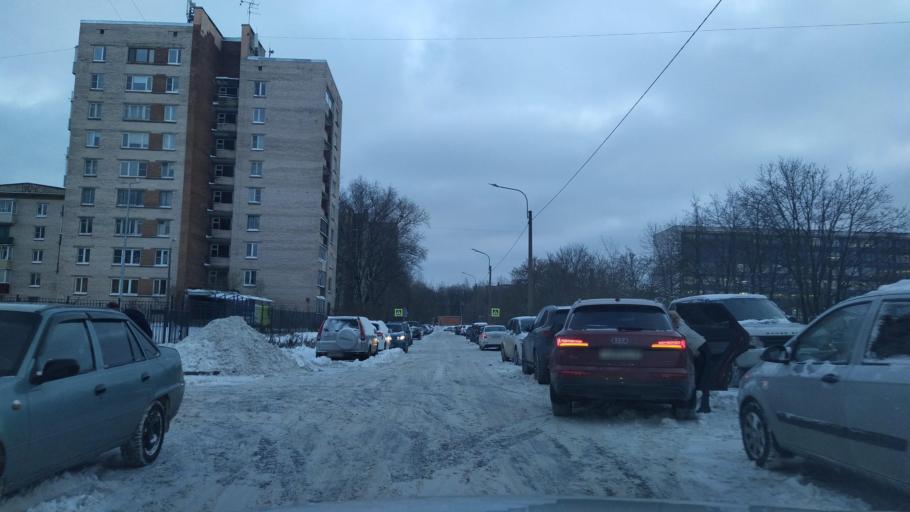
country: RU
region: St.-Petersburg
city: Sosnovka
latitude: 60.0133
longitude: 30.3619
